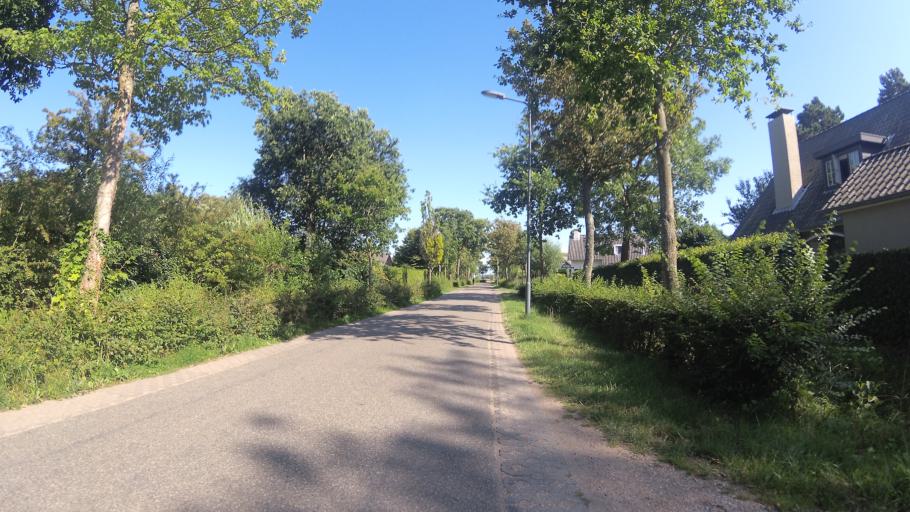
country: NL
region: Zeeland
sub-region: Gemeente Middelburg
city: Middelburg
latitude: 51.5647
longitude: 3.5066
